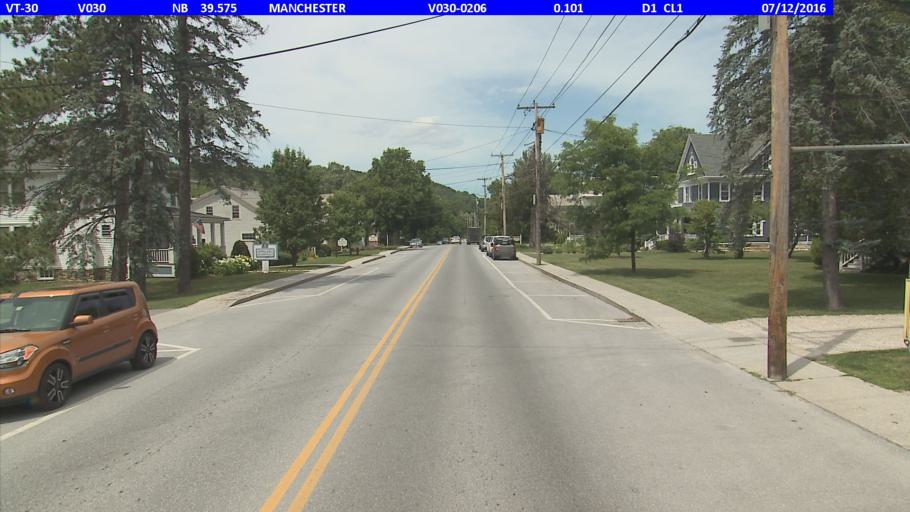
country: US
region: Vermont
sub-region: Bennington County
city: Manchester Center
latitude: 43.1783
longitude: -73.0572
